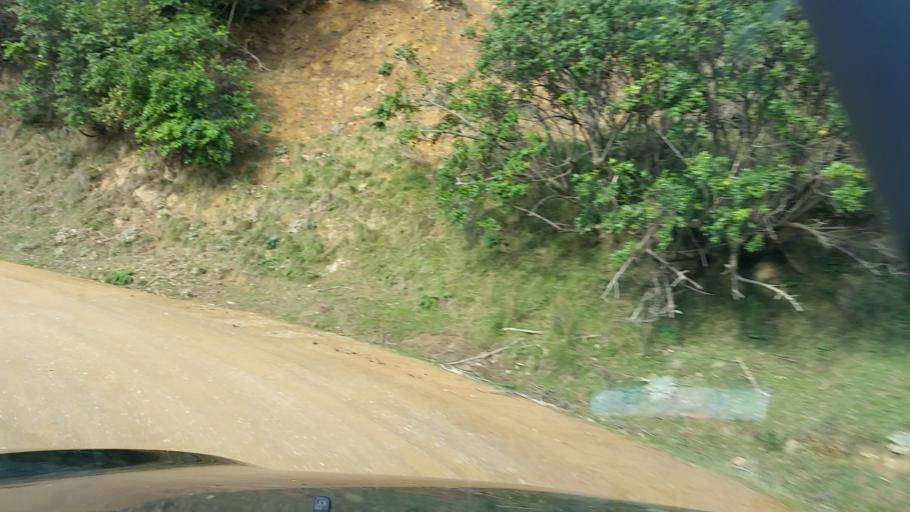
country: NZ
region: Marlborough
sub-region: Marlborough District
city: Picton
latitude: -40.9894
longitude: 173.8421
